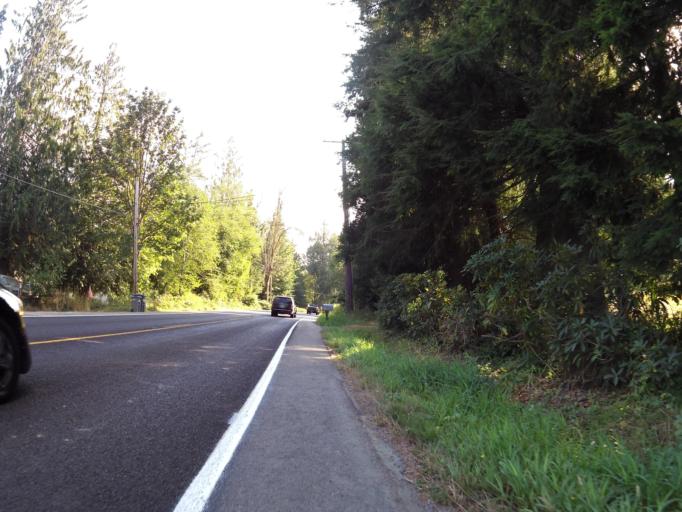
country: US
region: Washington
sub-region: Mason County
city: Belfair
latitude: 47.5057
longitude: -122.7960
